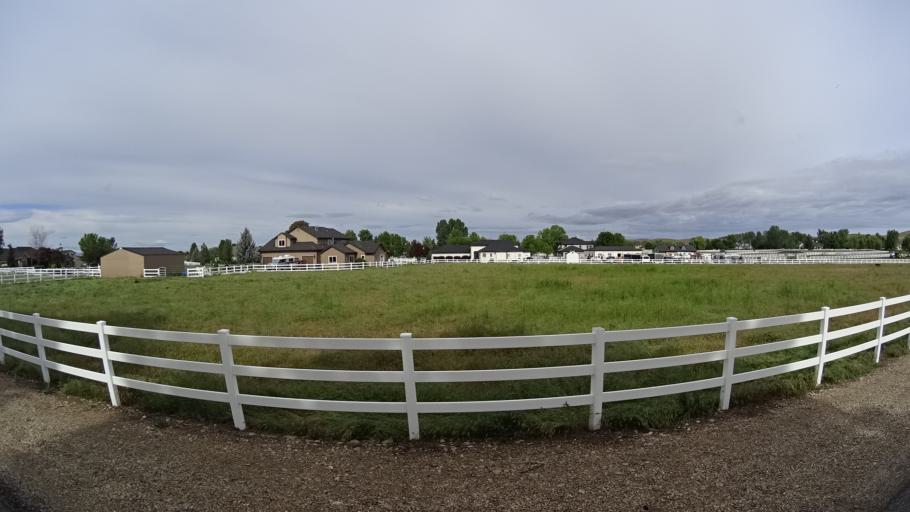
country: US
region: Idaho
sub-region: Ada County
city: Eagle
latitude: 43.7262
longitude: -116.4032
